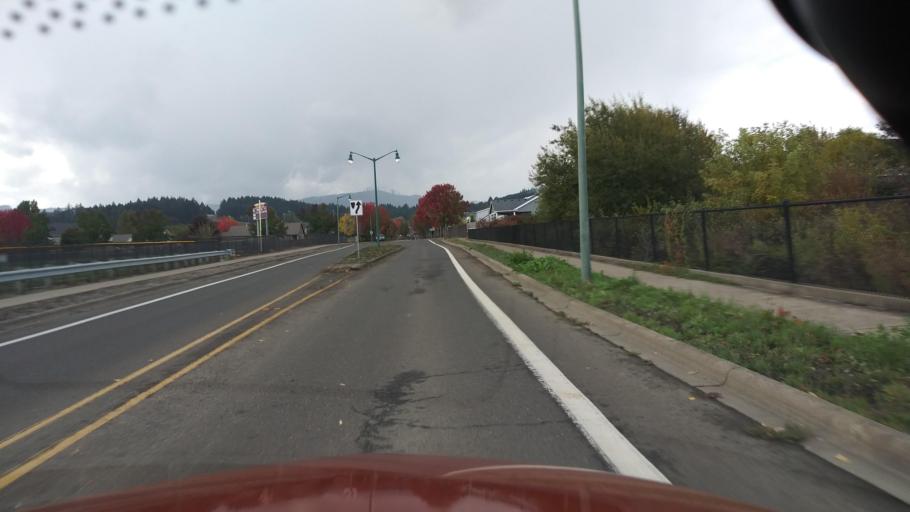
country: US
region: Oregon
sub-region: Washington County
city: Forest Grove
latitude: 45.5392
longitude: -123.1219
